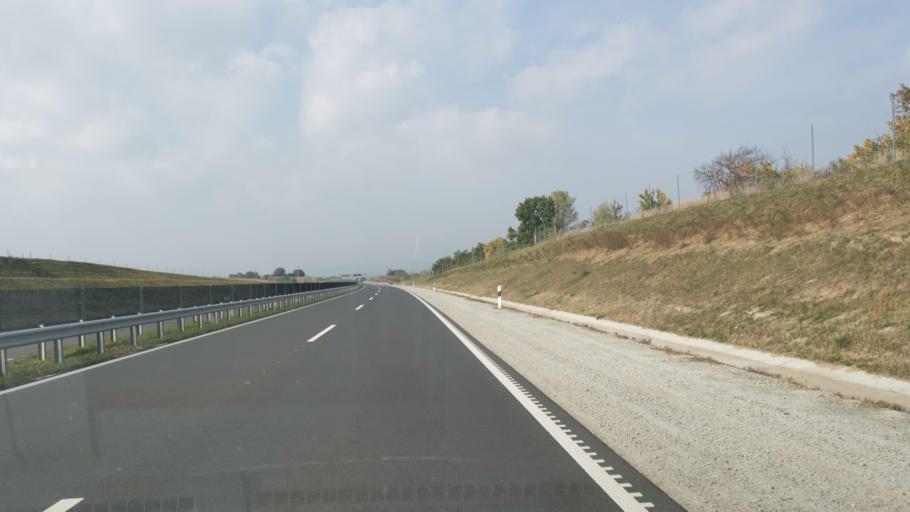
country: HU
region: Gyor-Moson-Sopron
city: Nagycenk
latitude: 47.5998
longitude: 16.6904
